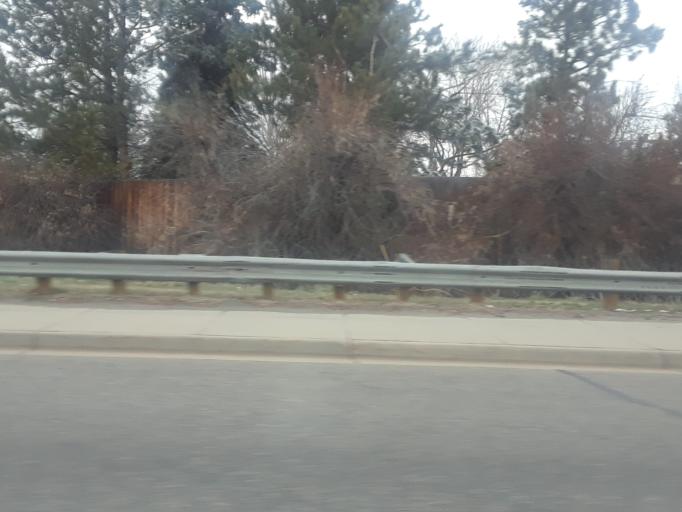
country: US
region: Colorado
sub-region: Douglas County
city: Acres Green
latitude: 39.5661
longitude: -104.8884
